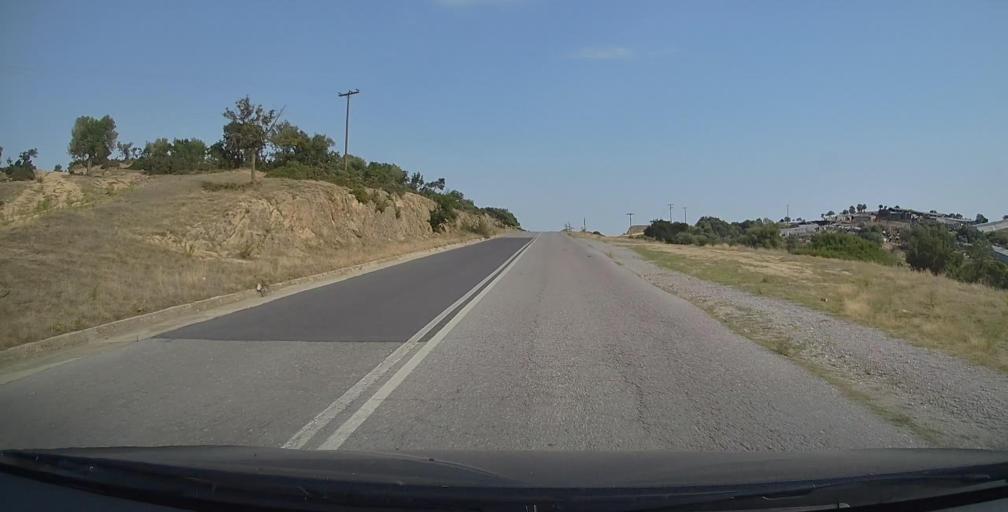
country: GR
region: Central Macedonia
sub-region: Nomos Chalkidikis
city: Sykia
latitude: 40.0159
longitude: 23.9868
